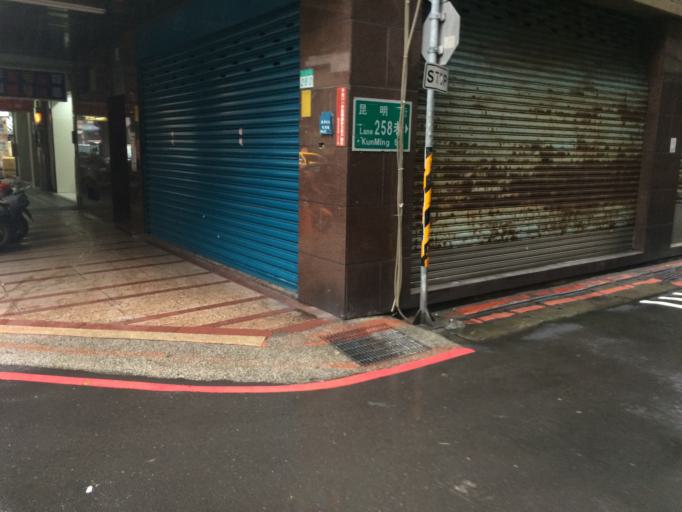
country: TW
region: Taipei
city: Taipei
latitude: 25.0395
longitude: 121.5042
